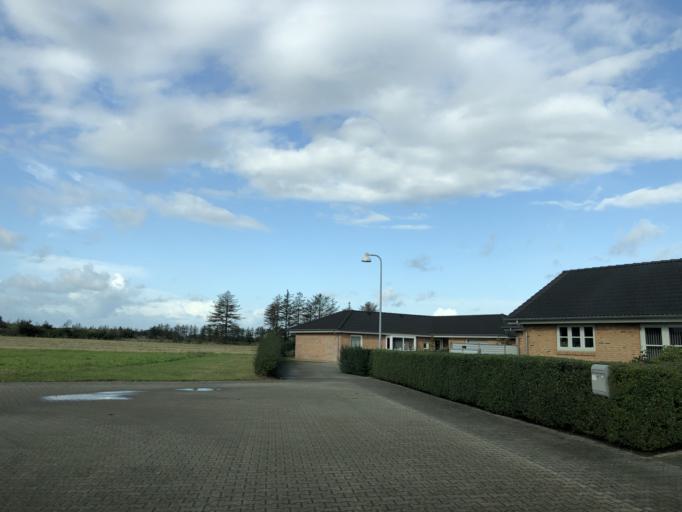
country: DK
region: Central Jutland
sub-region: Holstebro Kommune
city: Ulfborg
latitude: 56.2752
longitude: 8.3044
